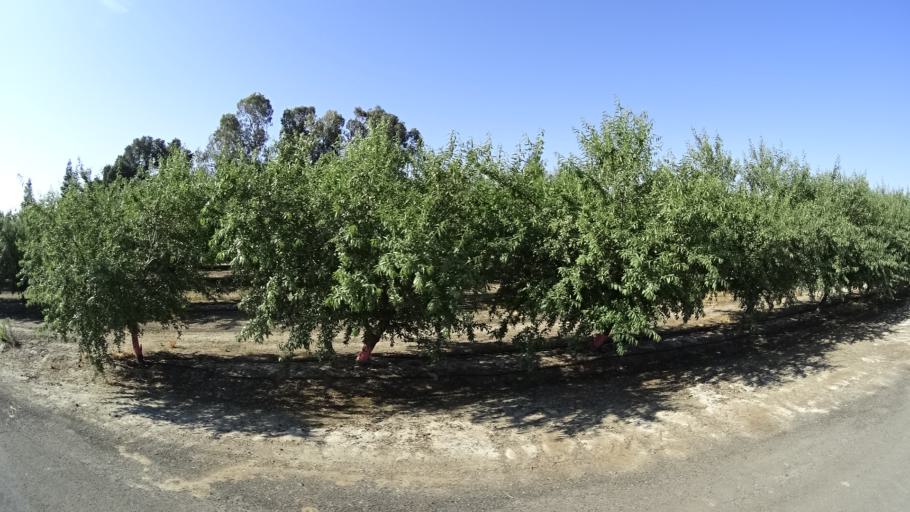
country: US
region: California
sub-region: Fresno County
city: Riverdale
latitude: 36.3657
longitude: -119.8260
